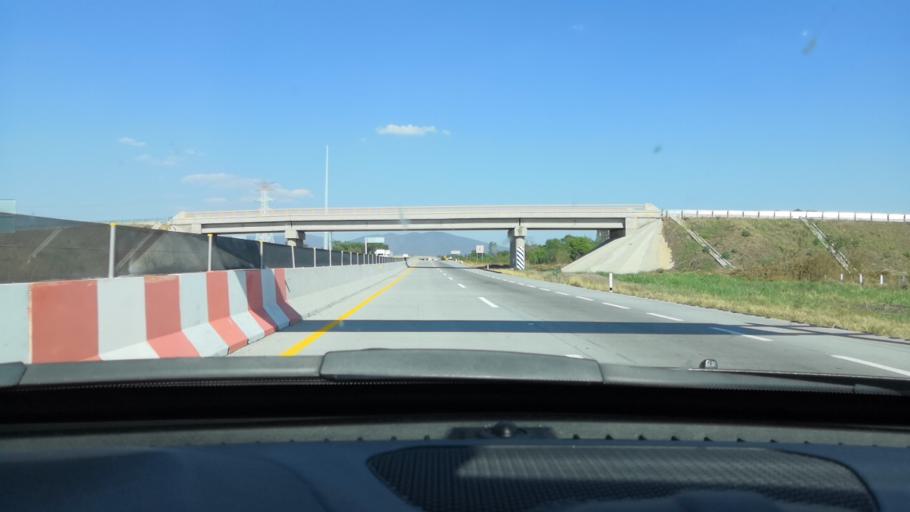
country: MX
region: Jalisco
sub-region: Ixtlahuacan de los Membrillos
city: Los Cedros
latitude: 20.4086
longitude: -103.2240
